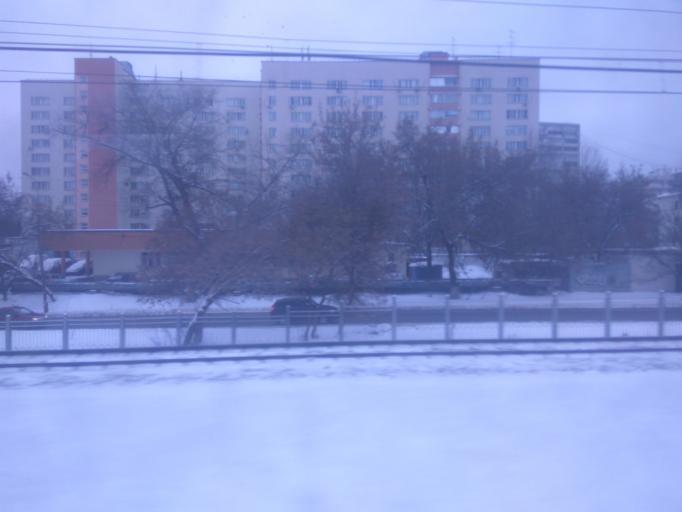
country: RU
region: Moscow
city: Lyublino
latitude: 55.6801
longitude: 37.7316
